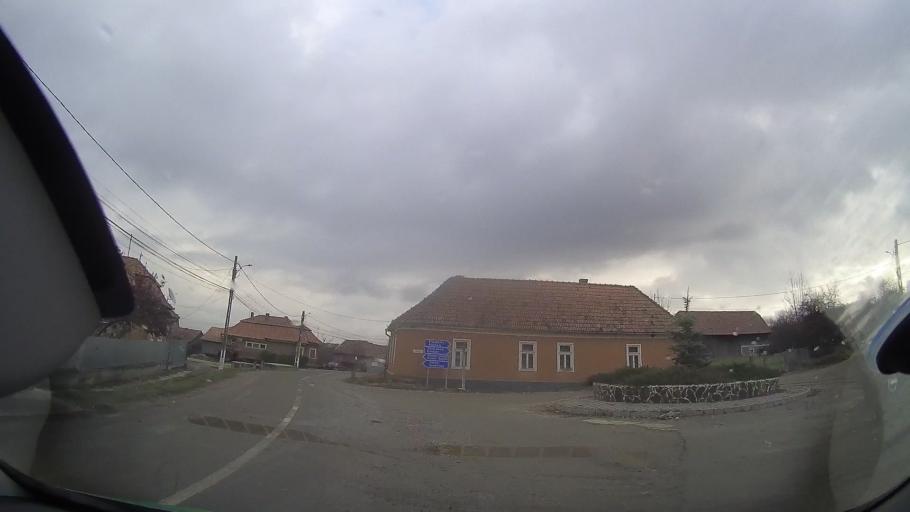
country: RO
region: Cluj
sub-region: Comuna Moldovenesti
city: Moldovenesti
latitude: 46.5006
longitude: 23.6643
